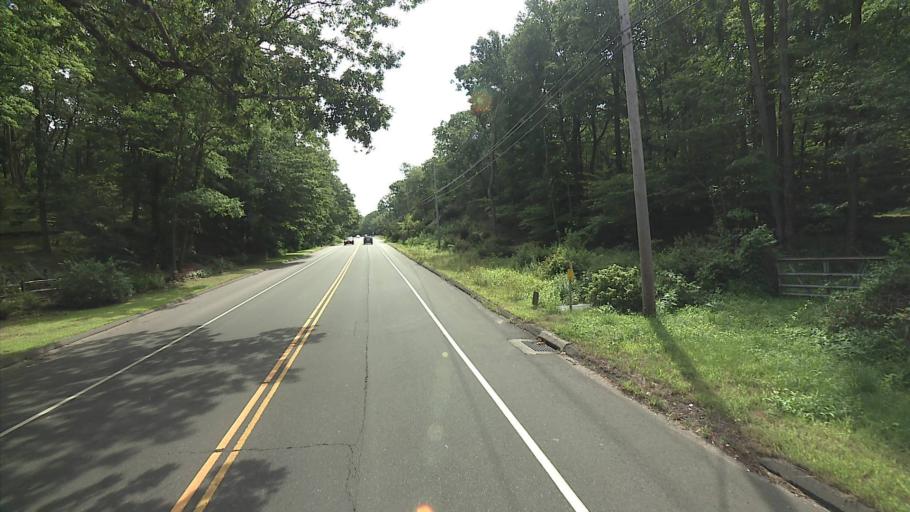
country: US
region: Connecticut
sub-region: New Haven County
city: Woodbridge
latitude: 41.3311
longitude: -72.9942
